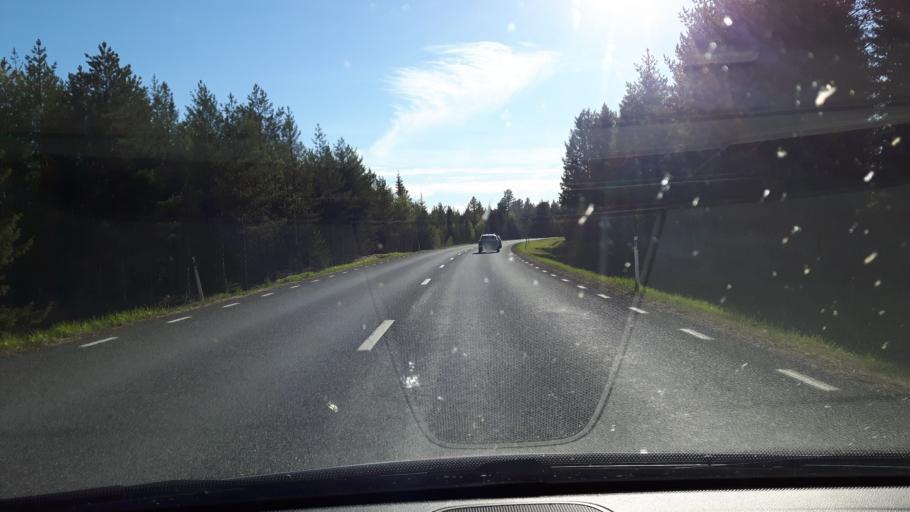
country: SE
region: Jaemtland
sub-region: OEstersunds Kommun
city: Lit
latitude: 63.3937
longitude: 15.0244
